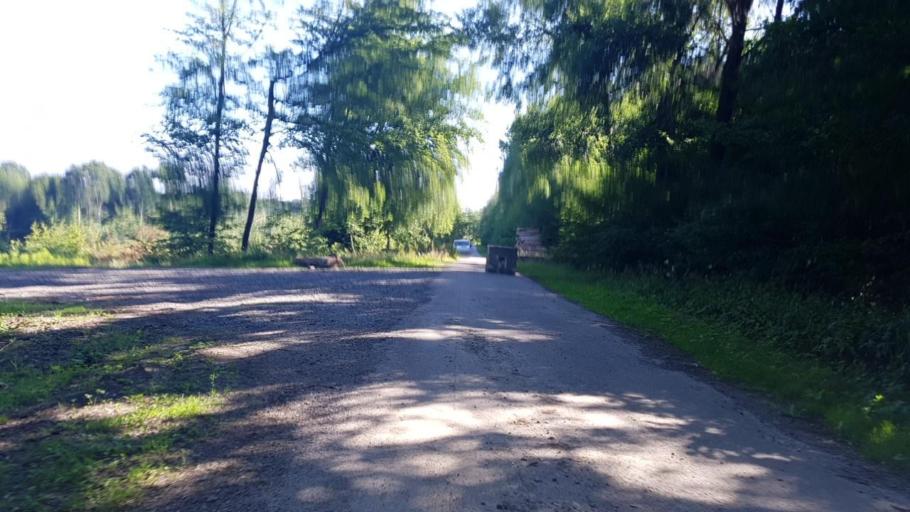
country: FR
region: Picardie
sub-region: Departement de l'Aisne
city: Hirson
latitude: 49.9407
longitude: 4.0959
